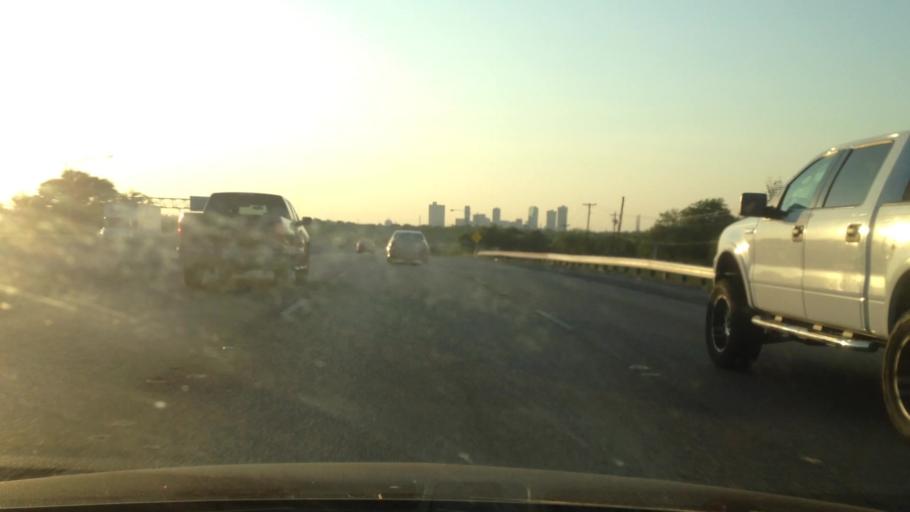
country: US
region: Texas
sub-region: Tarrant County
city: Fort Worth
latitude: 32.7197
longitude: -97.2892
